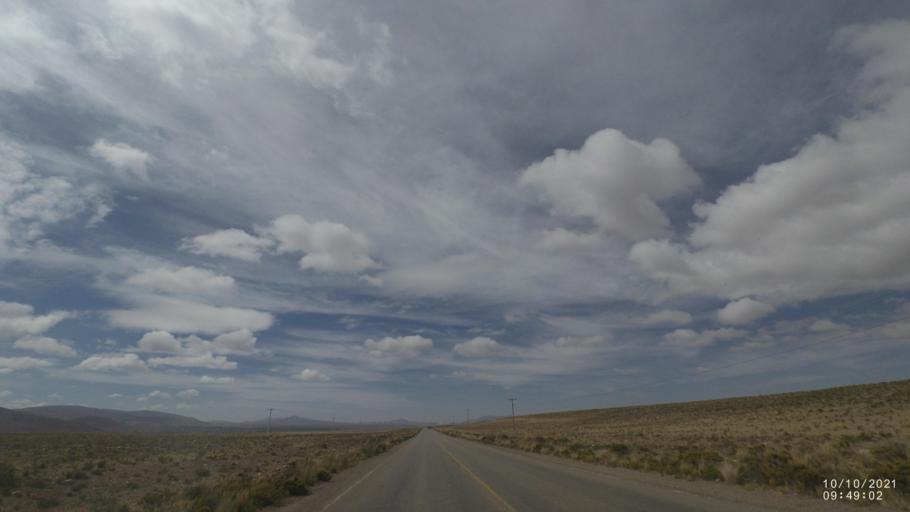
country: BO
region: La Paz
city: Quime
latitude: -17.2200
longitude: -67.3408
